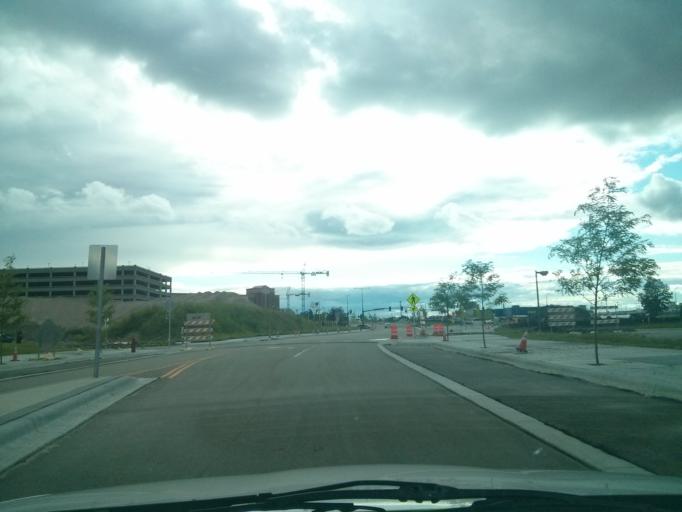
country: US
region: Minnesota
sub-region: Hennepin County
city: Richfield
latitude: 44.8567
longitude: -93.2349
